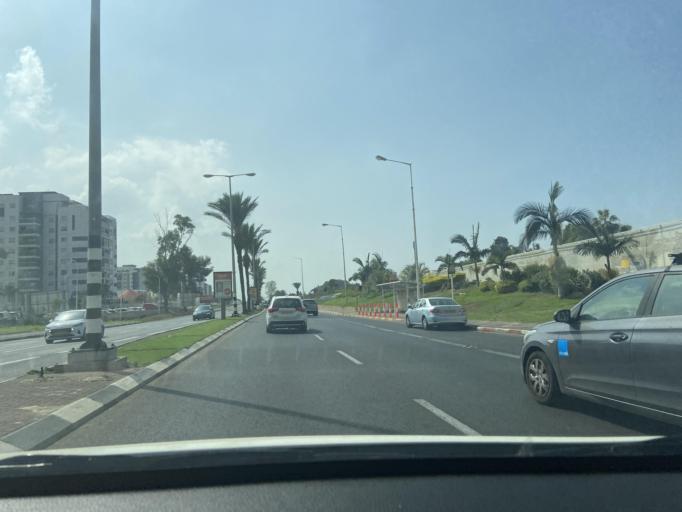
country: IL
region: Northern District
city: Nahariya
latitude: 33.0053
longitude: 35.0993
